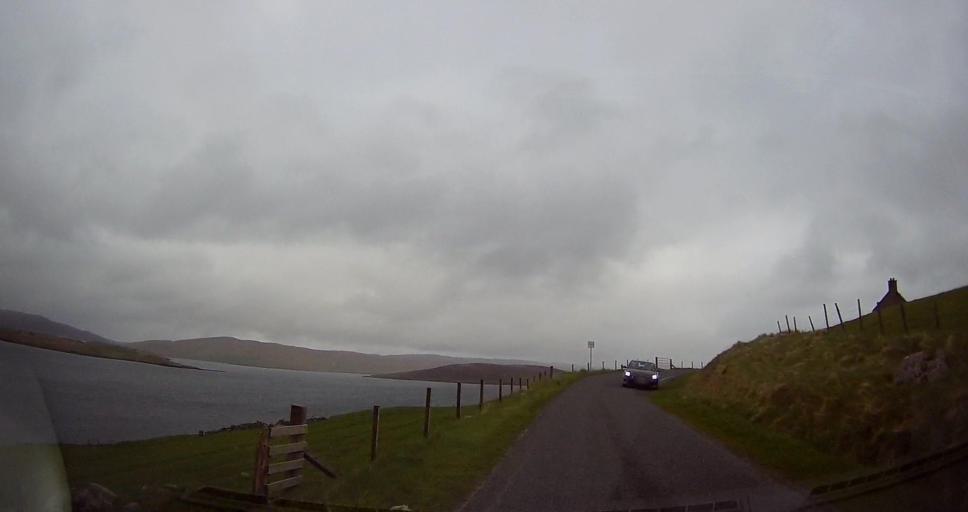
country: GB
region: Scotland
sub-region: Shetland Islands
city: Lerwick
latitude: 60.3742
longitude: -1.3826
